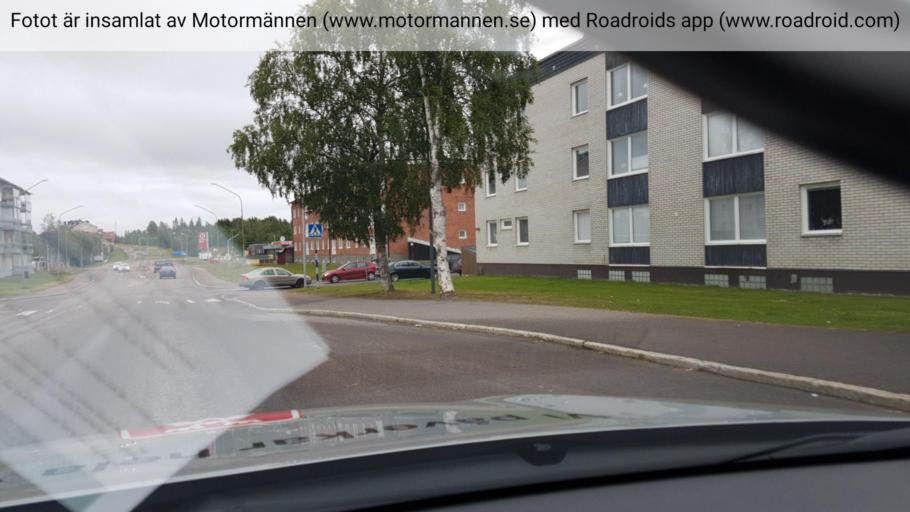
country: SE
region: Norrbotten
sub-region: Gallivare Kommun
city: Gaellivare
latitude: 67.1363
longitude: 20.6559
